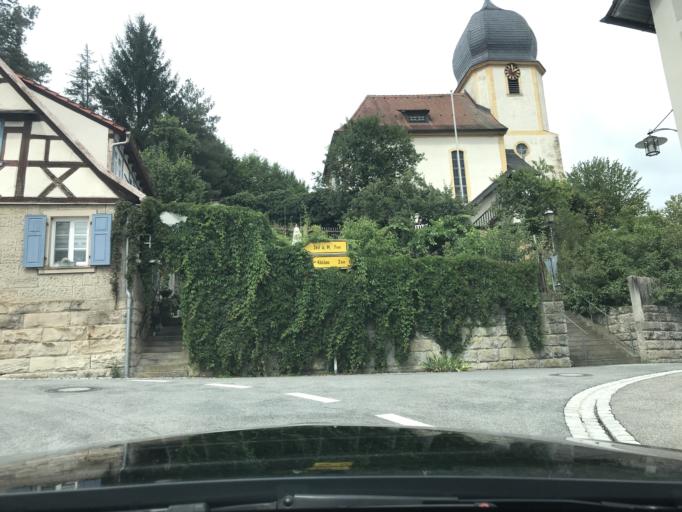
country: DE
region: Bavaria
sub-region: Regierungsbezirk Unterfranken
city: Breitbrunn
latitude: 50.0439
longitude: 10.6592
